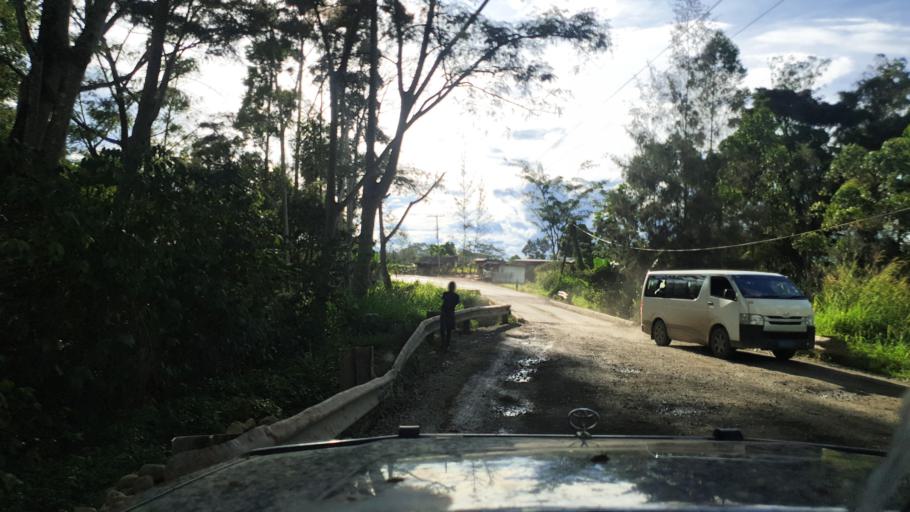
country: PG
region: Jiwaka
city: Minj
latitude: -5.8689
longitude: 144.6555
